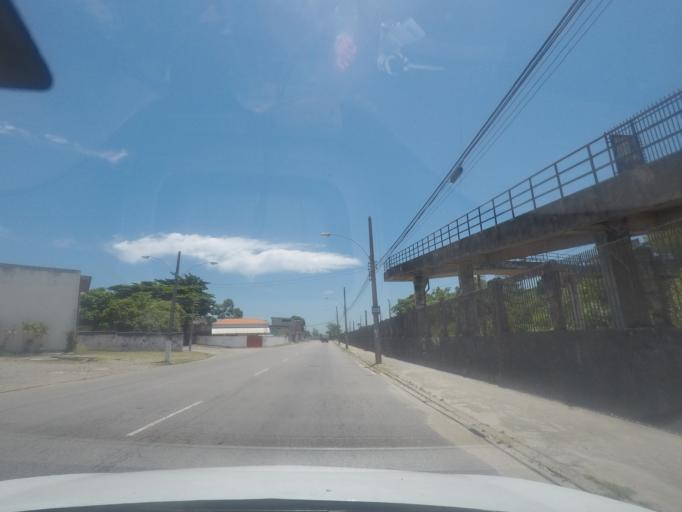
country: BR
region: Rio de Janeiro
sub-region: Itaguai
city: Itaguai
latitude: -22.9198
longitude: -43.6896
